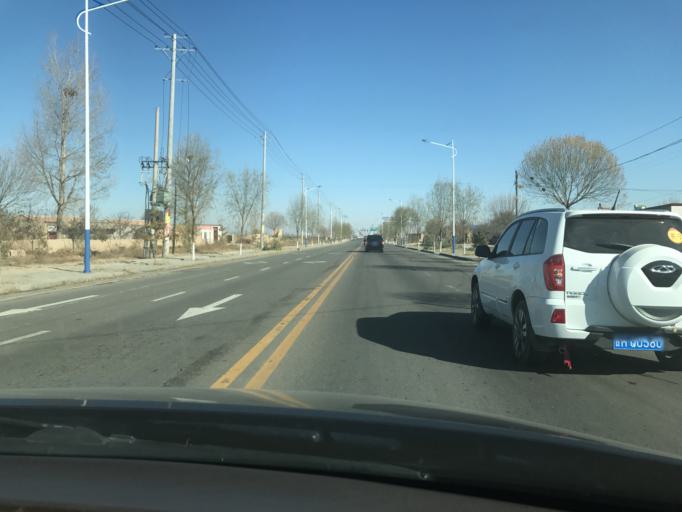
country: CN
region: Gansu Sheng
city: Gulang
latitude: 37.7016
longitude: 102.8487
